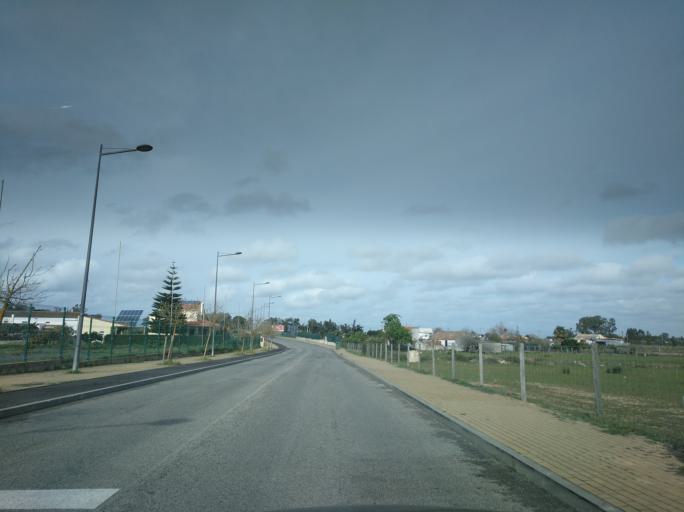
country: PT
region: Setubal
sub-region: Grandola
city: Grandola
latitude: 38.1854
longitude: -8.5639
